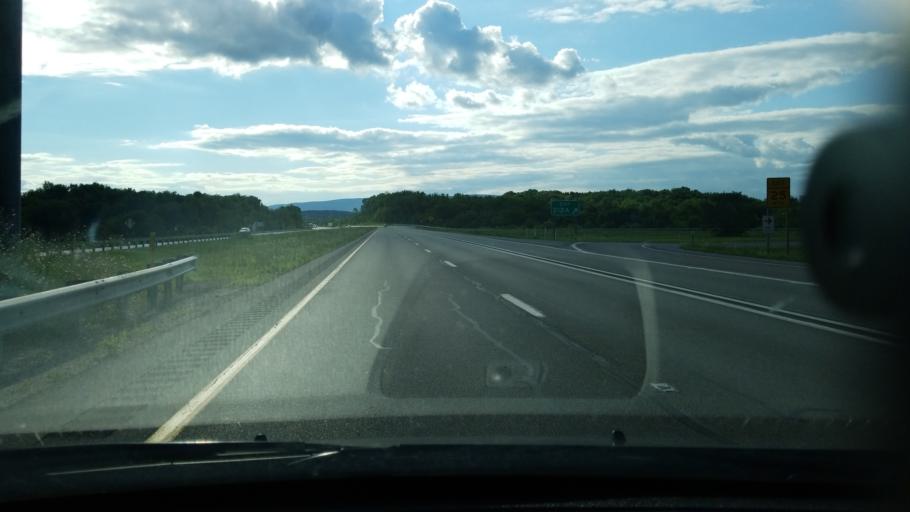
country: US
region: Pennsylvania
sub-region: Union County
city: New Columbia
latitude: 41.0500
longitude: -76.8406
